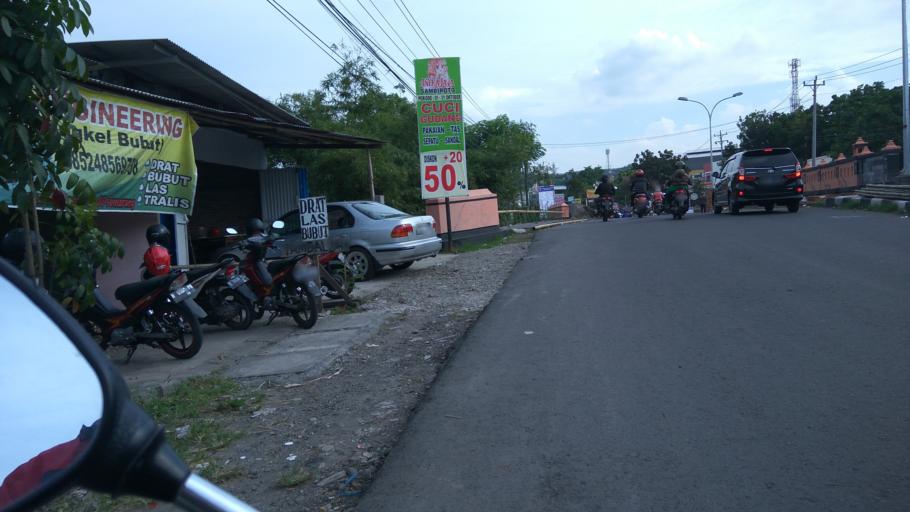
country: ID
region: Central Java
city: Semarang
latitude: -7.0279
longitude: 110.4594
